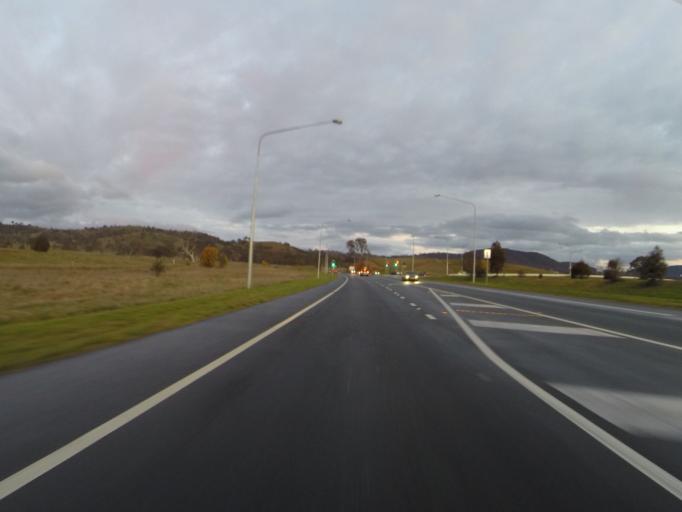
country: AU
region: Australian Capital Territory
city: Kaleen
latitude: -35.1994
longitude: 149.1645
